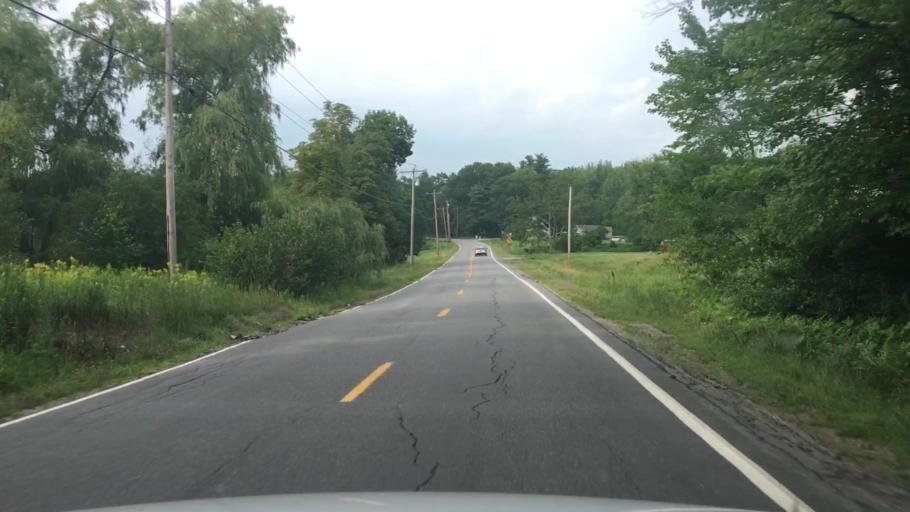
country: US
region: Maine
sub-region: Knox County
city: Washington
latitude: 44.2871
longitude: -69.3643
